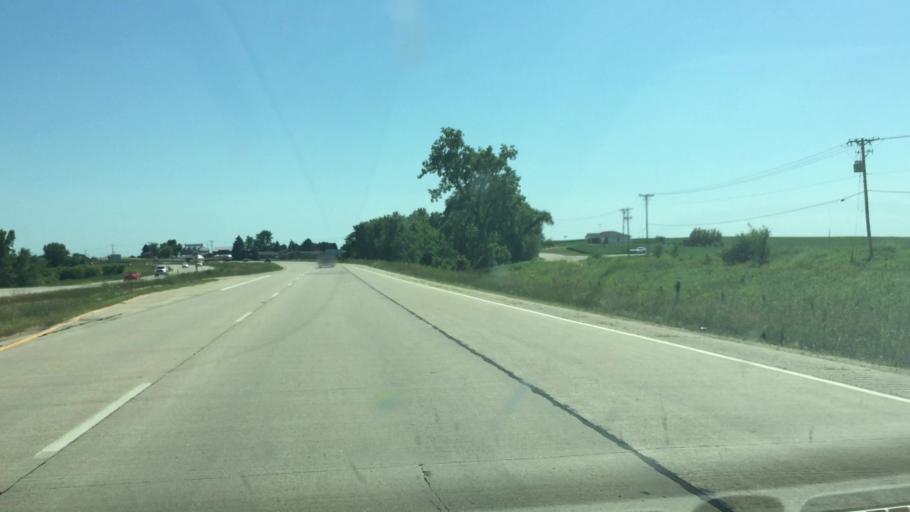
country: US
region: Wisconsin
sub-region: Grant County
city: Dickeyville
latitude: 42.5748
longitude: -90.6107
